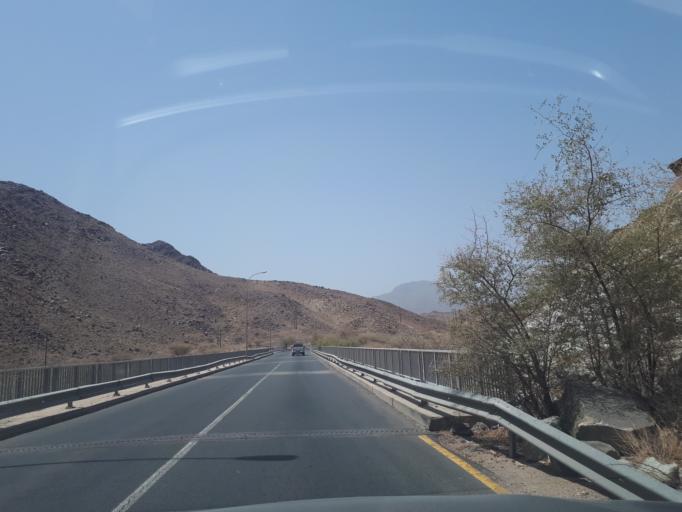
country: OM
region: Muhafazat ad Dakhiliyah
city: Sufalat Sama'il
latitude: 23.2462
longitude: 58.0869
